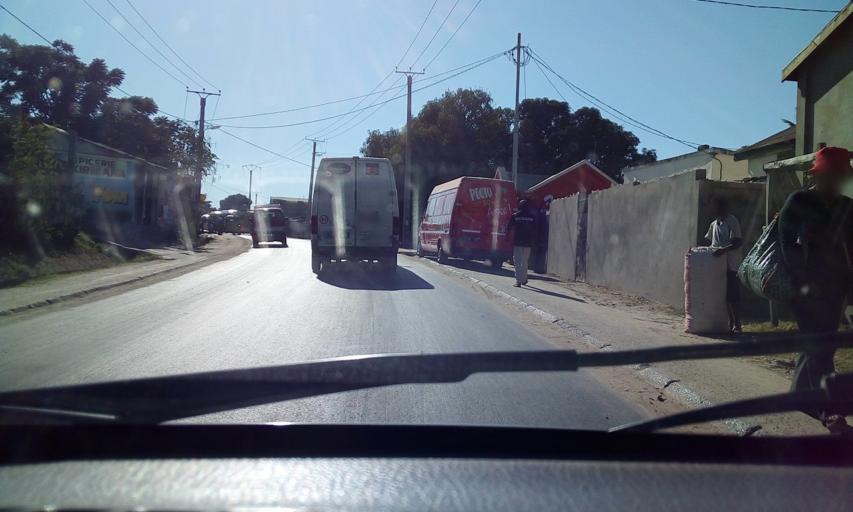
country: MG
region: Boeny
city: Mahajanga
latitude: -15.7163
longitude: 46.3352
